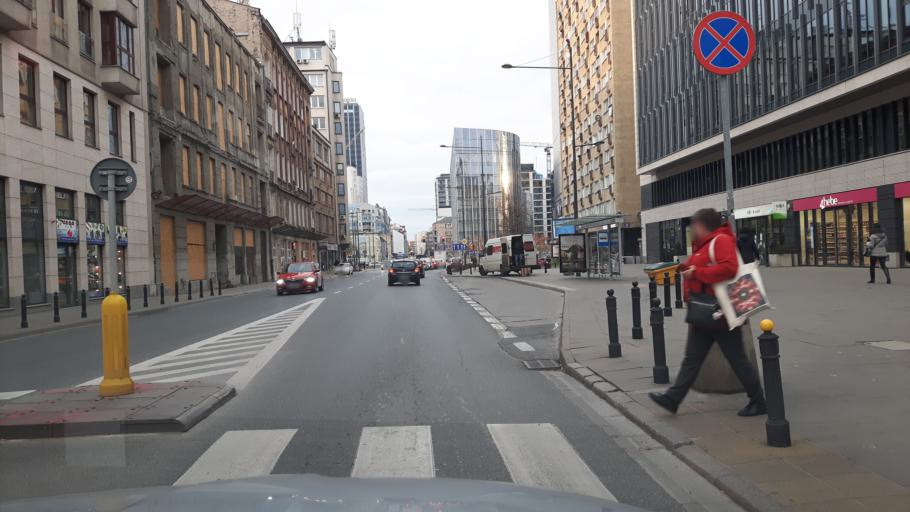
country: PL
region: Masovian Voivodeship
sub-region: Warszawa
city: Wola
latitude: 52.2303
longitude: 20.9936
